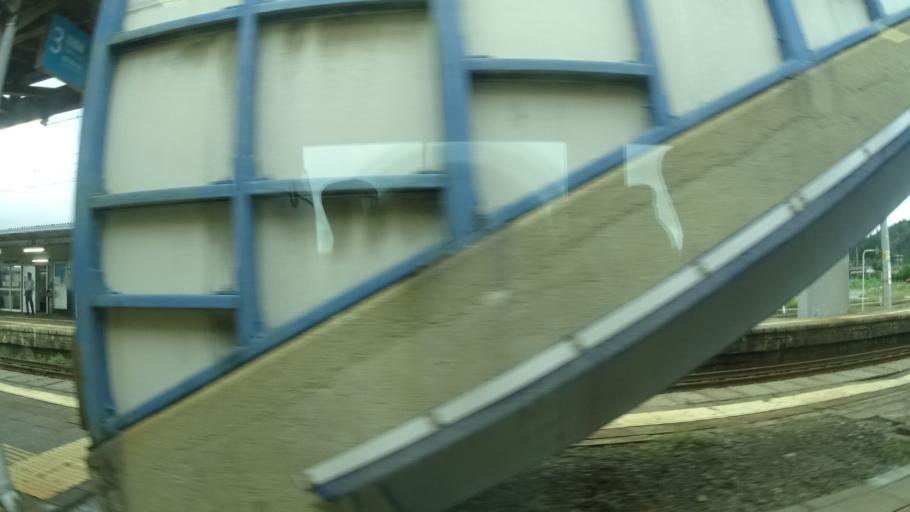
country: JP
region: Niigata
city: Murakami
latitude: 38.5140
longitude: 139.5309
